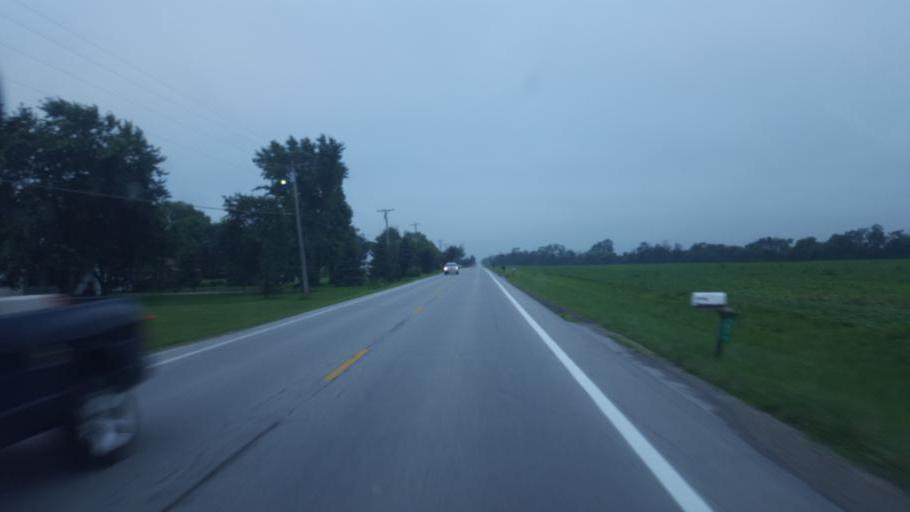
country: US
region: Ohio
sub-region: Madison County
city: Bethel
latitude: 39.6306
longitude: -83.3495
